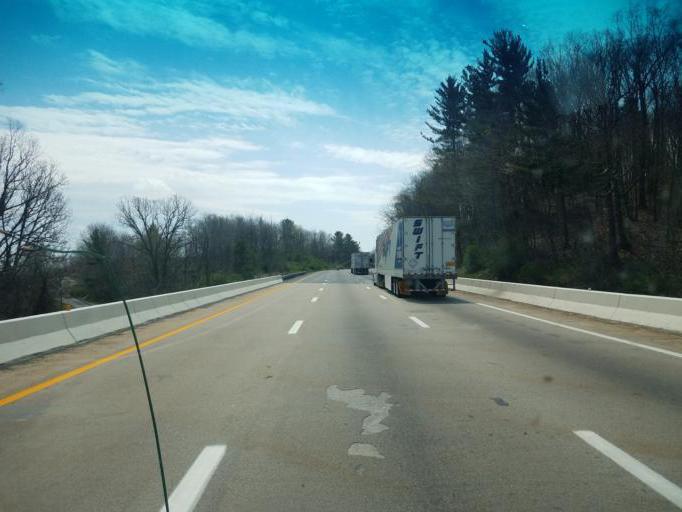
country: US
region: West Virginia
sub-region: Raleigh County
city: Shady Spring
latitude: 37.6503
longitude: -81.1125
